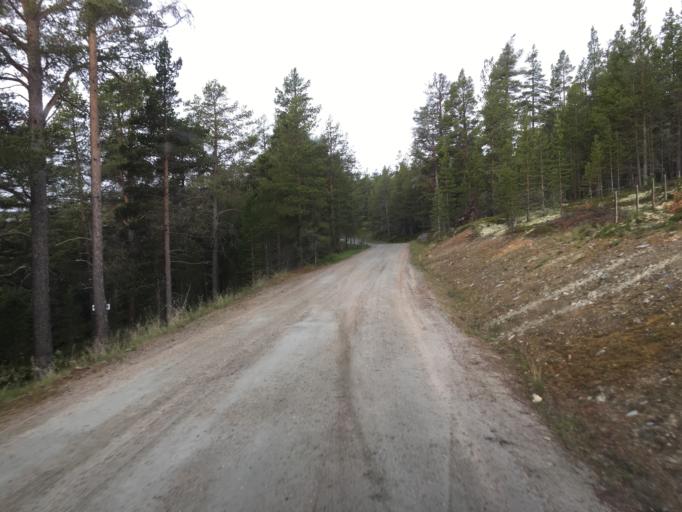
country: NO
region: Hedmark
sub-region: Folldal
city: Folldal
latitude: 62.0726
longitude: 9.9476
